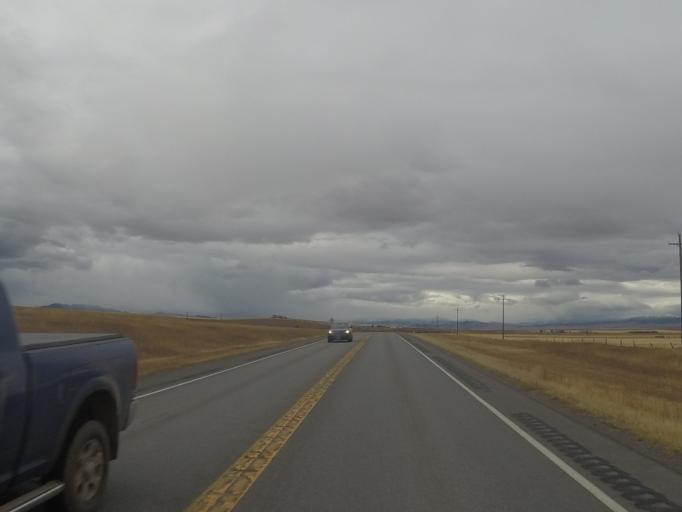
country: US
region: Montana
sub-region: Lewis and Clark County
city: East Helena
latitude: 46.5506
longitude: -111.7603
